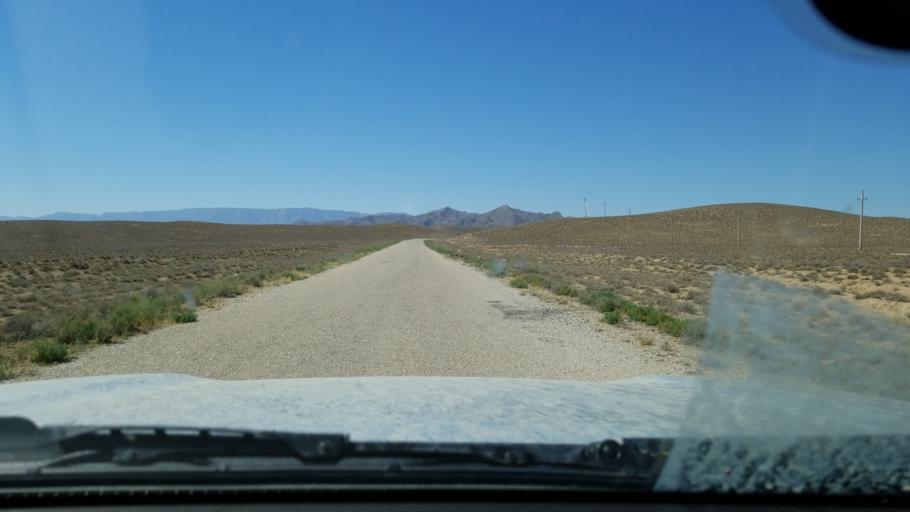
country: TM
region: Balkan
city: Balkanabat
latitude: 39.9145
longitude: 54.4297
